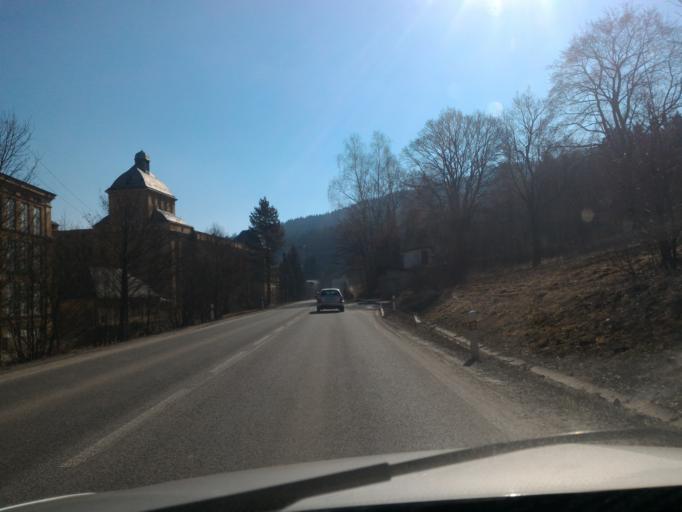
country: CZ
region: Liberecky
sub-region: Okres Jablonec nad Nisou
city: Tanvald
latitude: 50.7358
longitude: 15.2900
